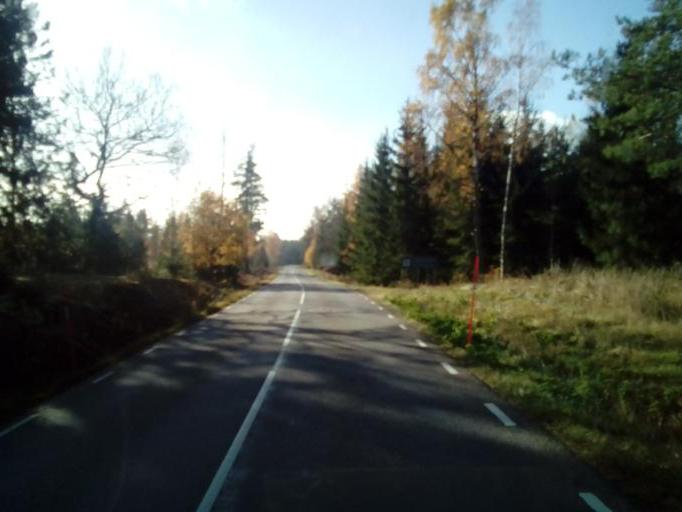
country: SE
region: Kalmar
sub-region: Vasterviks Kommun
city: Ankarsrum
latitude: 57.7664
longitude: 16.1369
